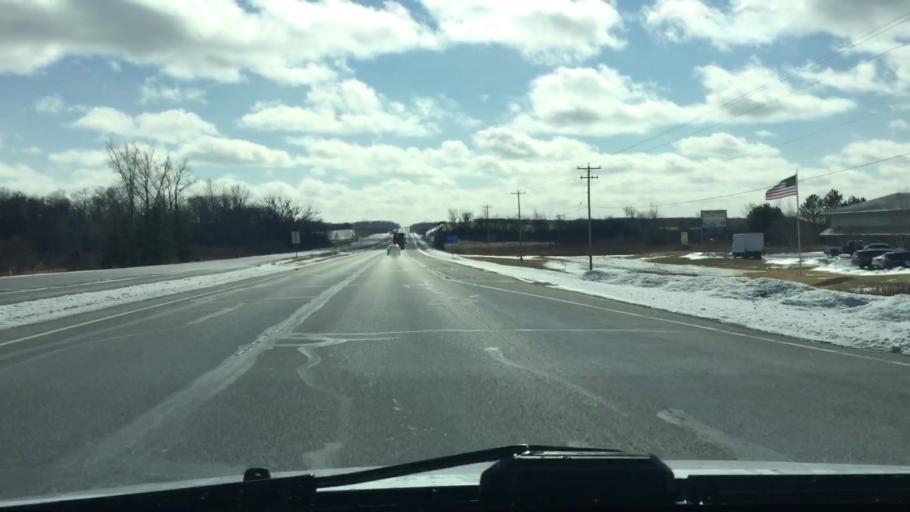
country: US
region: Wisconsin
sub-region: Waukesha County
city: Waukesha
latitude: 42.9706
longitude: -88.2278
